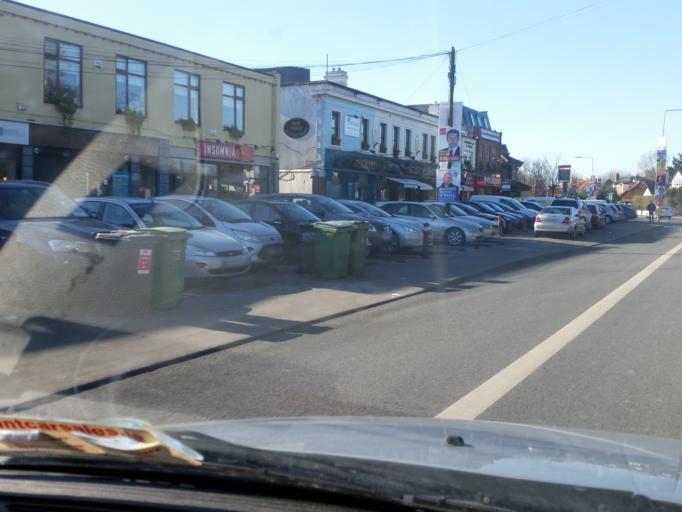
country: IE
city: Killester
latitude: 53.3710
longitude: -6.2056
